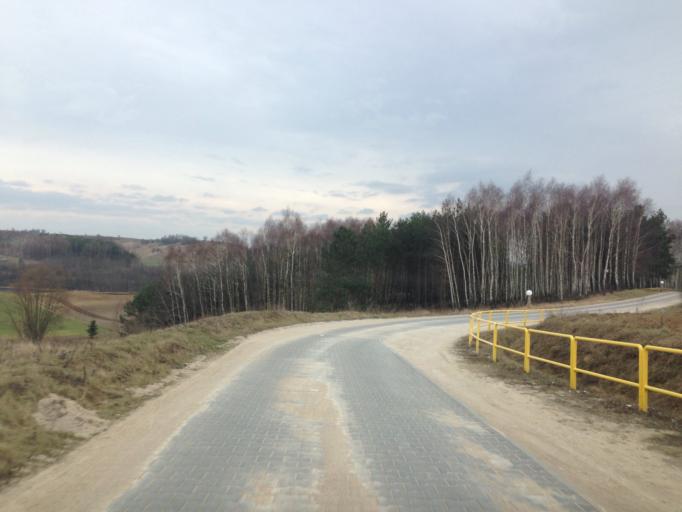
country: PL
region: Kujawsko-Pomorskie
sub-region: Powiat brodnicki
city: Brzozie
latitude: 53.3153
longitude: 19.5580
